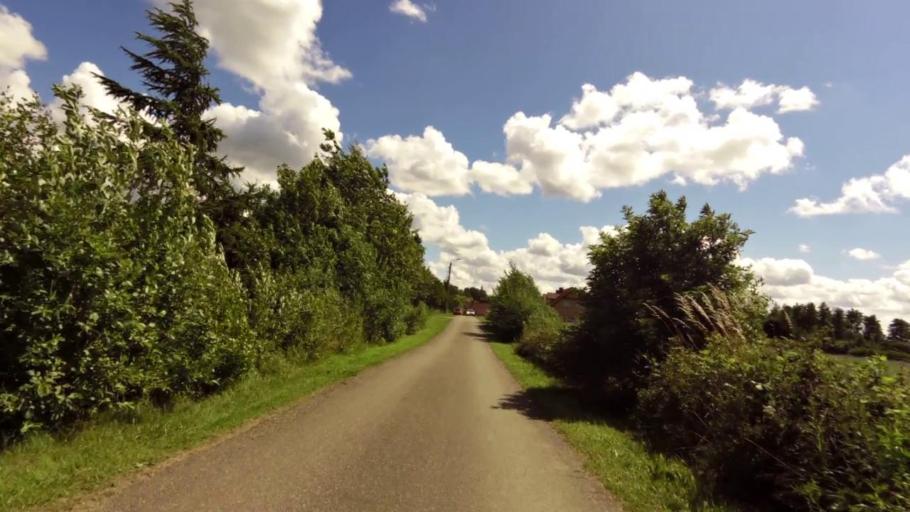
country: PL
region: West Pomeranian Voivodeship
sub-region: Powiat slawienski
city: Slawno
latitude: 54.5255
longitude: 16.6076
